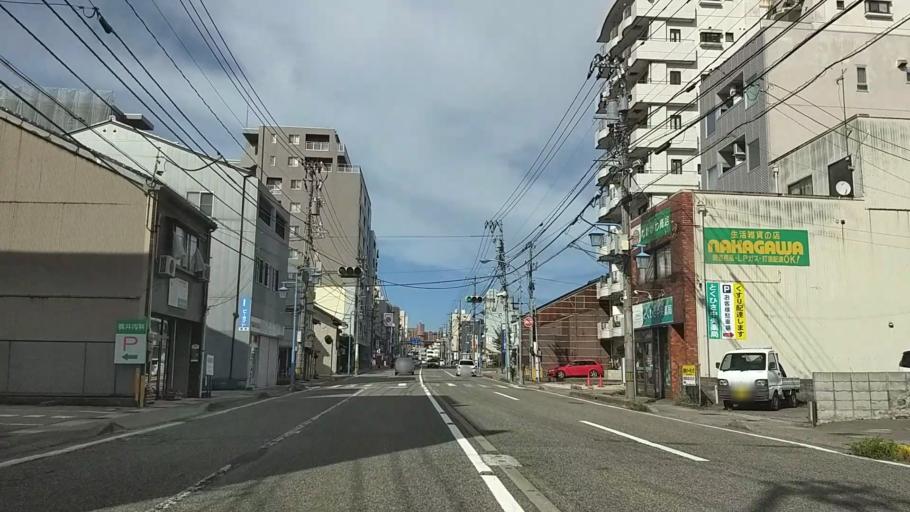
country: JP
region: Ishikawa
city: Nonoichi
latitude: 36.5544
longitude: 136.6471
